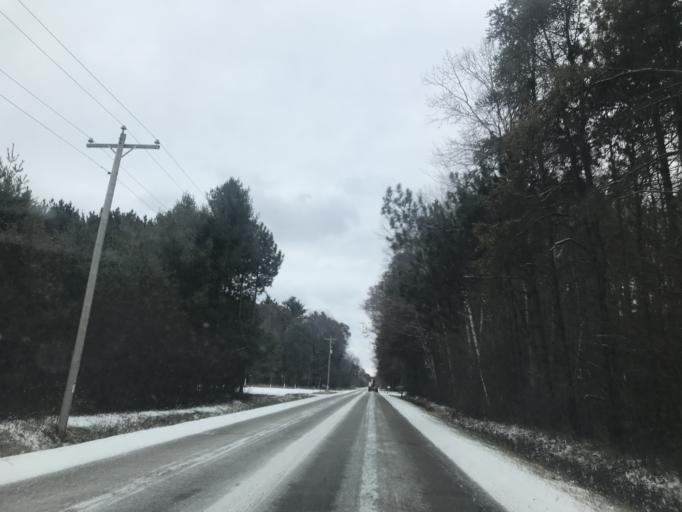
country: US
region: Wisconsin
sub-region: Marinette County
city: Marinette
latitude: 45.0631
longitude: -87.6591
